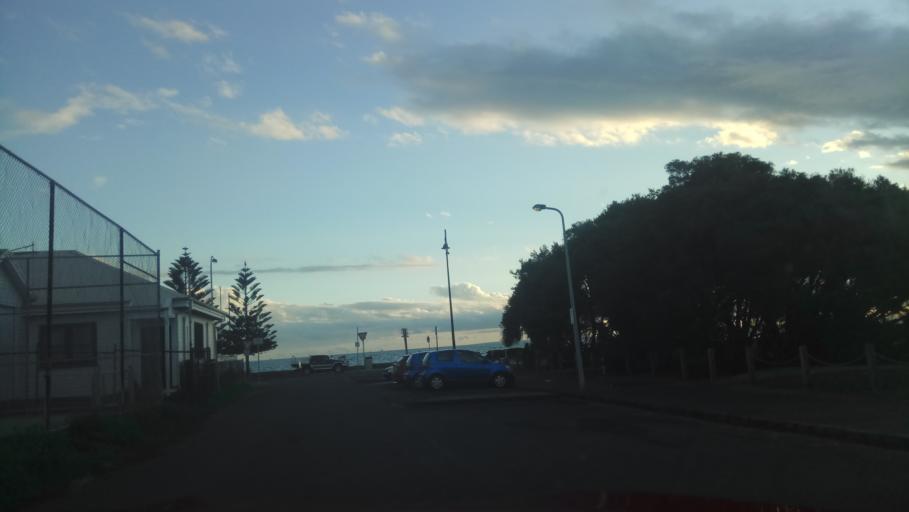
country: AU
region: Victoria
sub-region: Hobsons Bay
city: Williamstown
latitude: -37.8670
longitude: 144.8939
